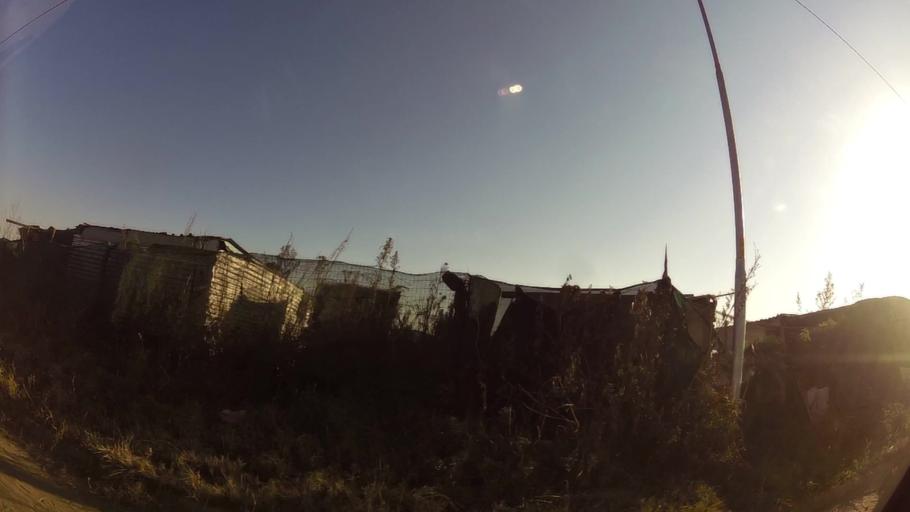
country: ZA
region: Gauteng
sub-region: City of Johannesburg Metropolitan Municipality
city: Midrand
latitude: -25.9178
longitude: 28.1039
